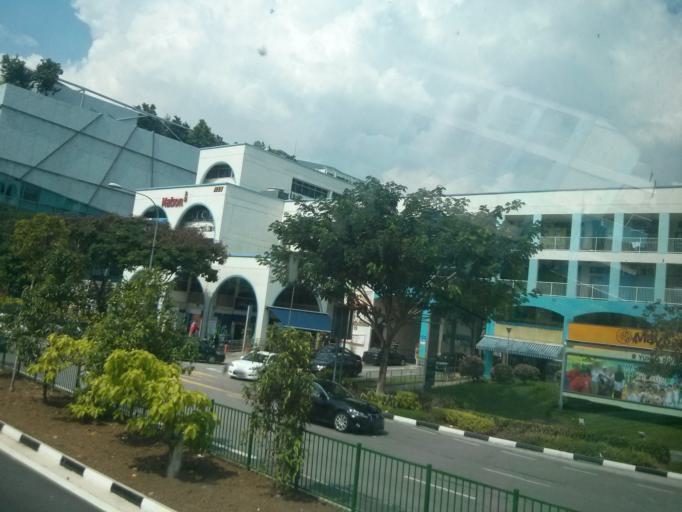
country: SG
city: Singapore
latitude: 1.3347
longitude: 103.7407
